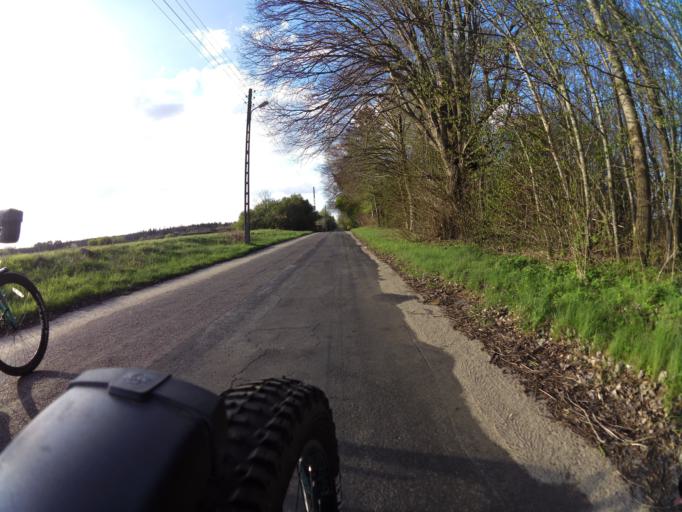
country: PL
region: West Pomeranian Voivodeship
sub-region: Powiat gryficki
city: Ploty
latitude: 53.7453
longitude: 15.2719
